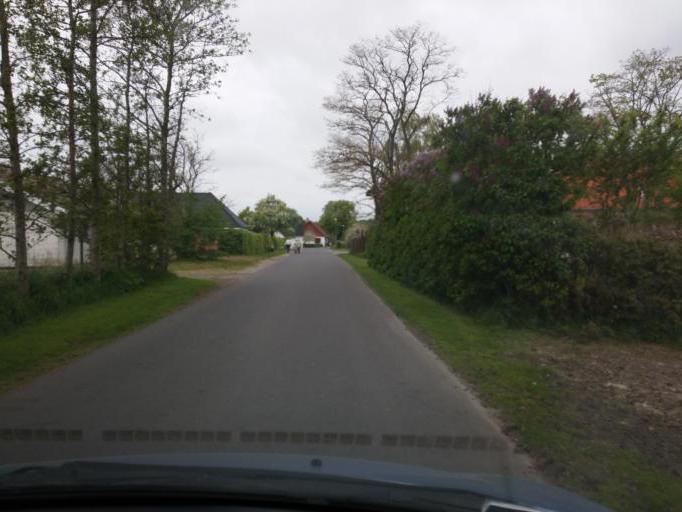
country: DK
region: South Denmark
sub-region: Odense Kommune
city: Bullerup
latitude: 55.4084
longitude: 10.5137
